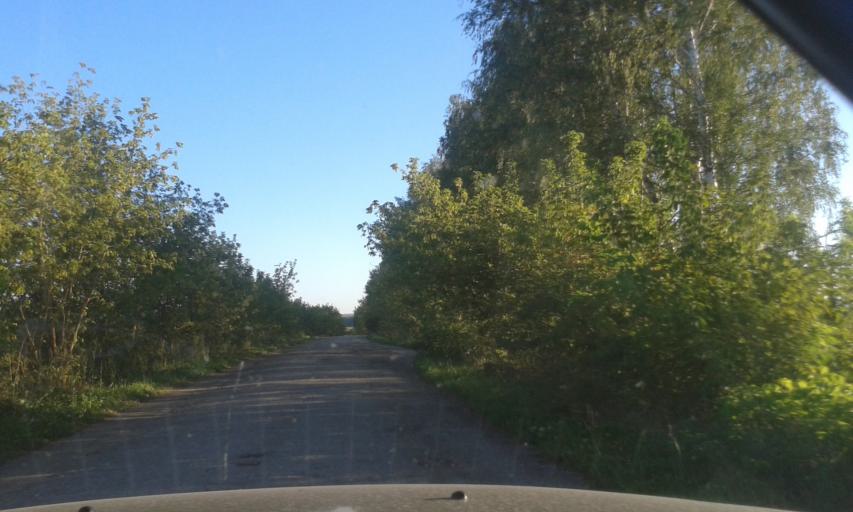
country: RU
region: Tula
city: Krapivna
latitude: 54.1284
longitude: 37.1561
